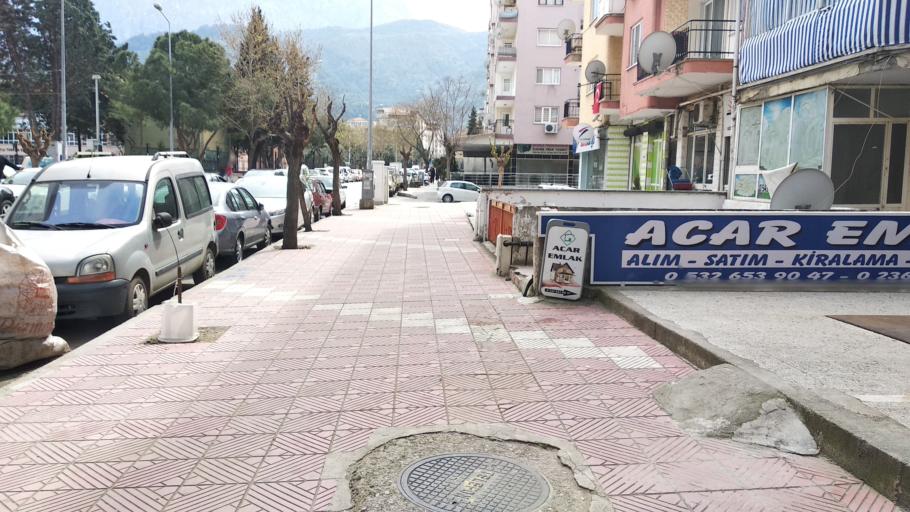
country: TR
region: Manisa
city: Manisa
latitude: 38.6174
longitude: 27.4186
